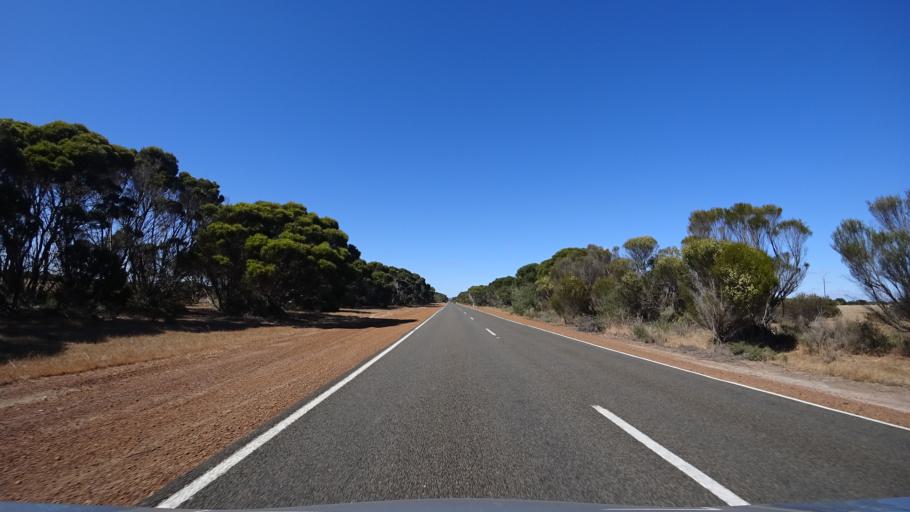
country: AU
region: South Australia
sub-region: Kangaroo Island
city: Kingscote
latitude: -35.7033
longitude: 137.5683
